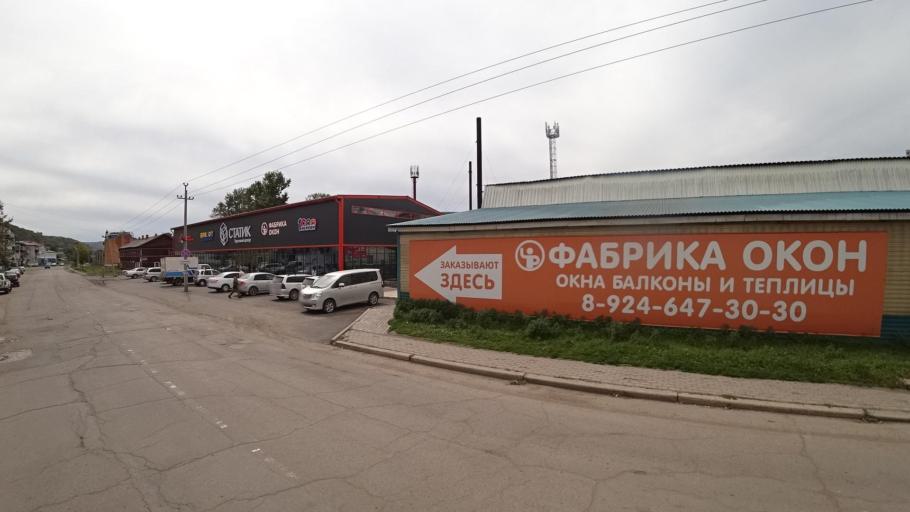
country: RU
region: Jewish Autonomous Oblast
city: Khingansk
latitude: 49.0112
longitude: 131.0571
